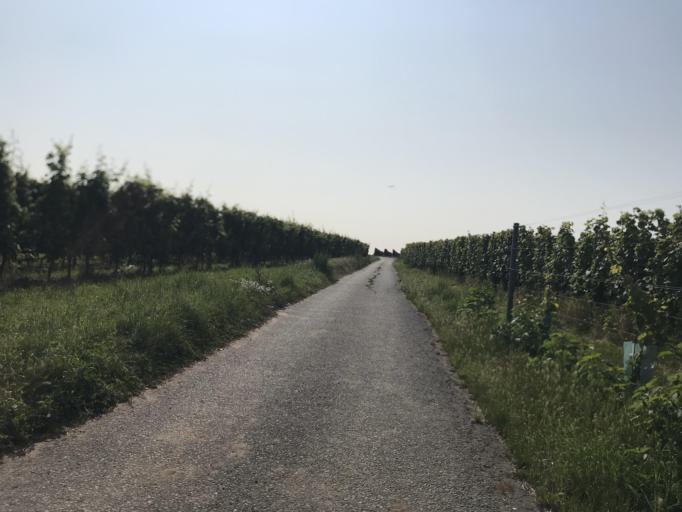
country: DE
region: Hesse
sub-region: Regierungsbezirk Darmstadt
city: Hochheim am Main
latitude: 50.0124
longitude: 8.3223
